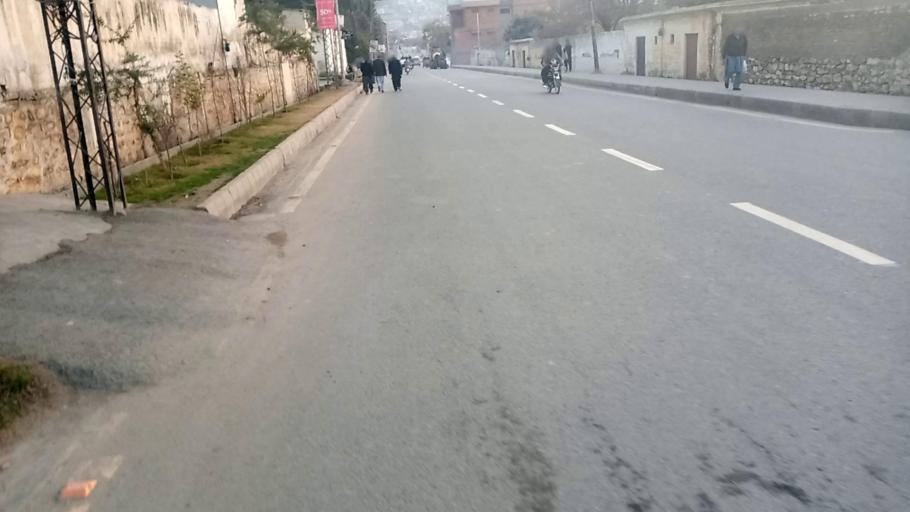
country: PK
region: Khyber Pakhtunkhwa
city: Saidu Sharif
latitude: 34.7556
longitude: 72.3604
